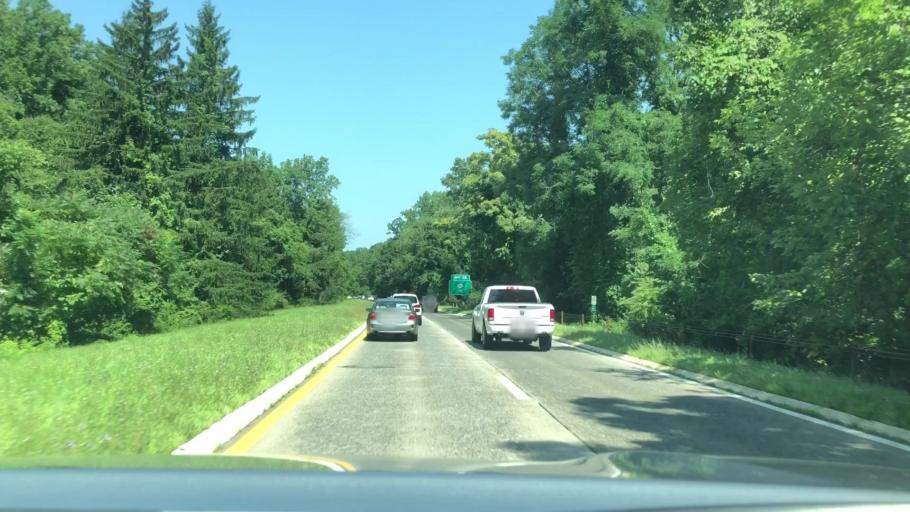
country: US
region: New York
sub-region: Rockland County
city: Pomona
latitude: 41.1666
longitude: -74.0290
